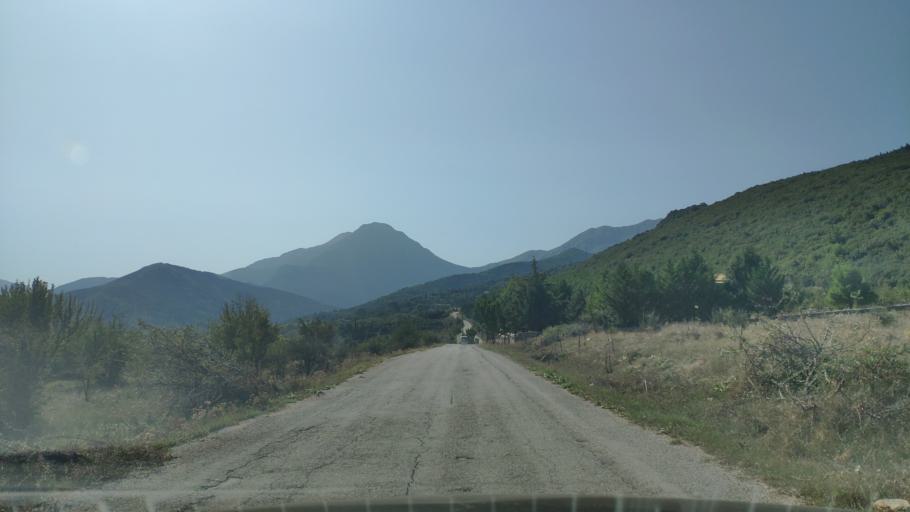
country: GR
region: West Greece
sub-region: Nomos Achaias
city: Aiyira
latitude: 37.9544
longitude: 22.3384
